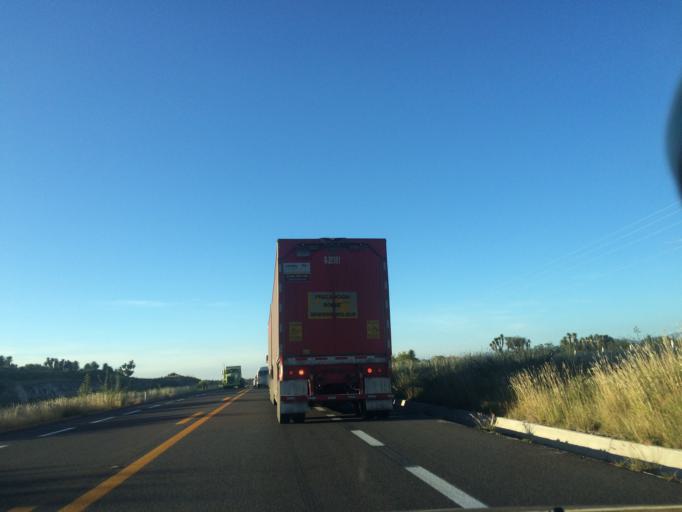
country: MX
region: Puebla
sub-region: Tehuacan
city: Magdalena Cuayucatepec
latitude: 18.5838
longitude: -97.4672
